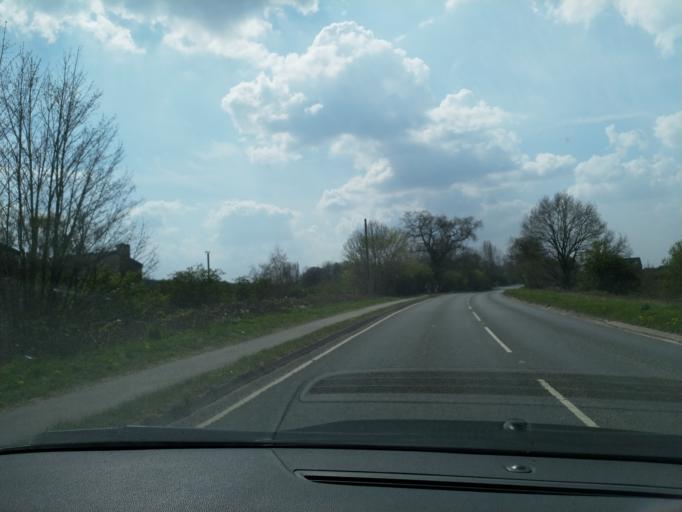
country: GB
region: England
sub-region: Warwickshire
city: Ryton on Dunsmore
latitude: 52.3550
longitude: -1.4444
